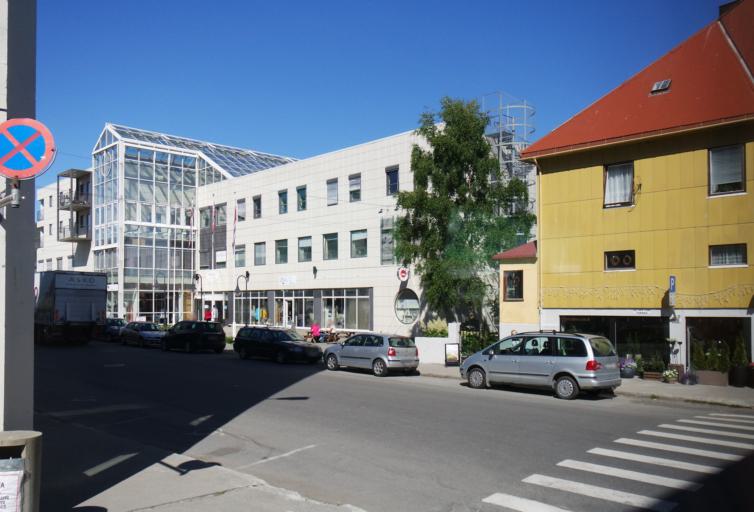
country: NO
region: Nordland
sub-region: Vagan
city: Svolvaer
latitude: 68.2321
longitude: 14.5626
